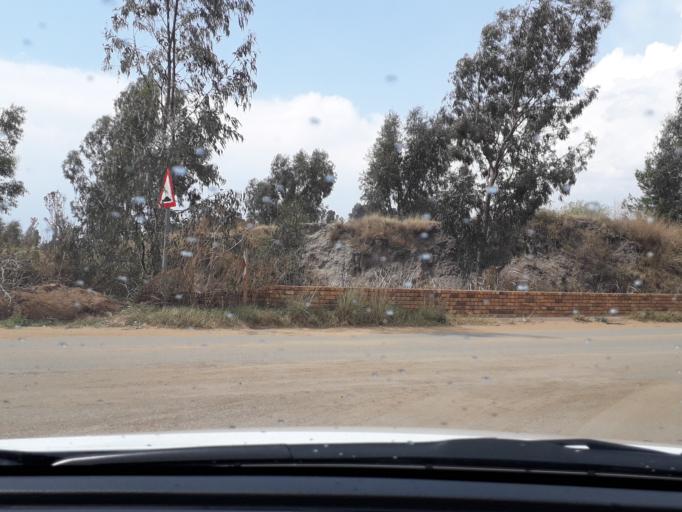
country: ZA
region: Gauteng
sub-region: West Rand District Municipality
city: Muldersdriseloop
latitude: -26.0040
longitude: 27.8528
